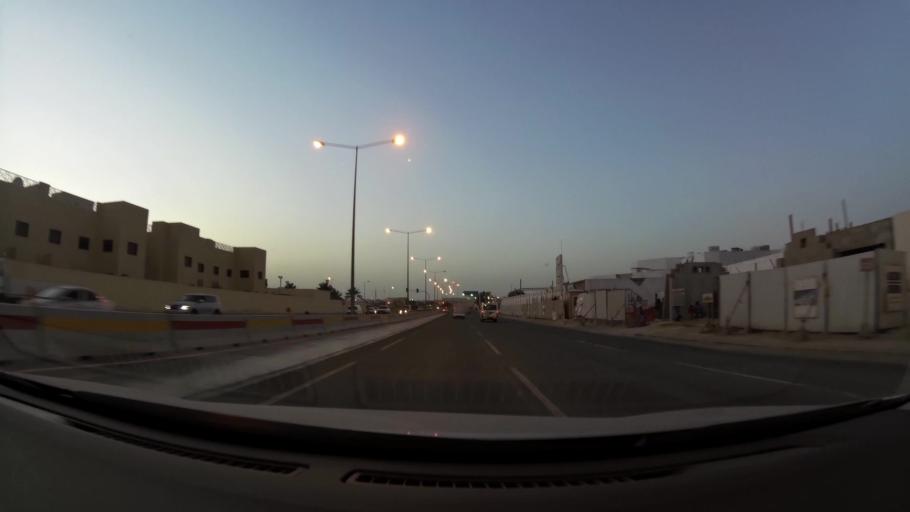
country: QA
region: Baladiyat ar Rayyan
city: Ar Rayyan
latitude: 25.3091
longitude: 51.4627
